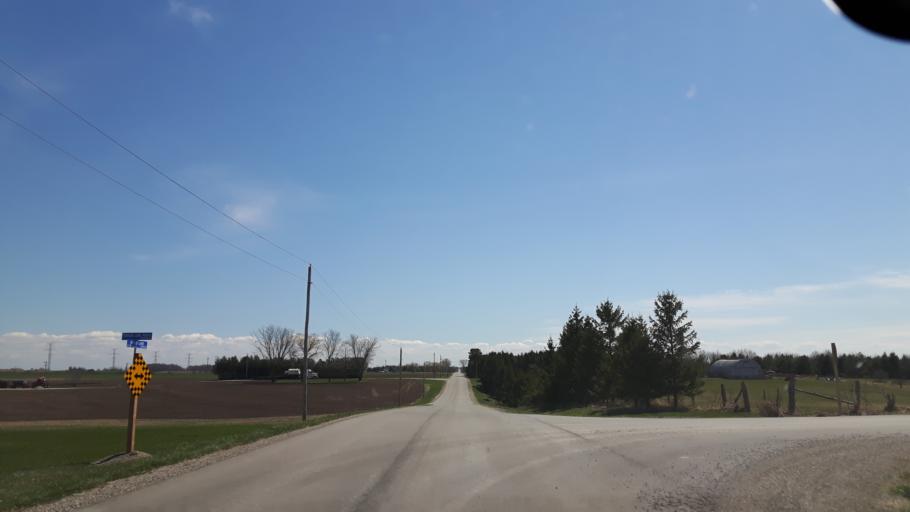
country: CA
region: Ontario
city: Goderich
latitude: 43.6242
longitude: -81.6440
